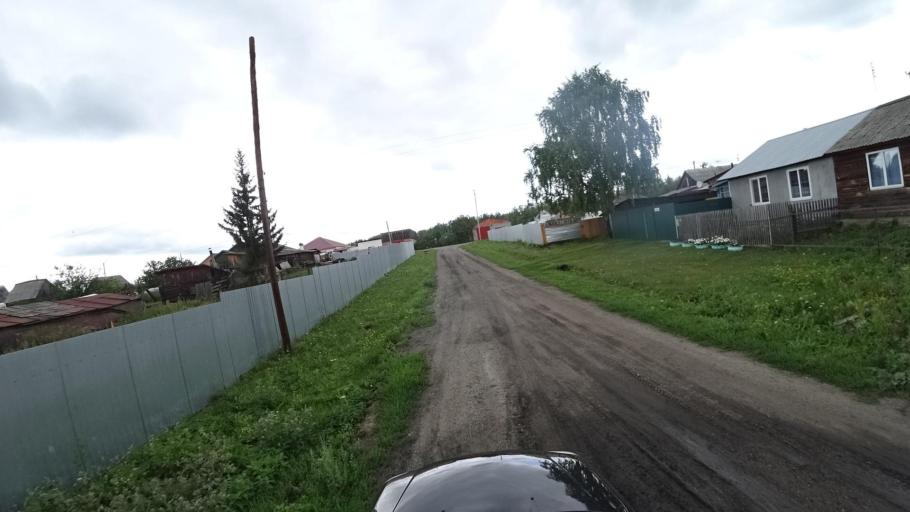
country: RU
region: Sverdlovsk
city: Kamyshlov
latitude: 56.8551
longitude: 62.6892
